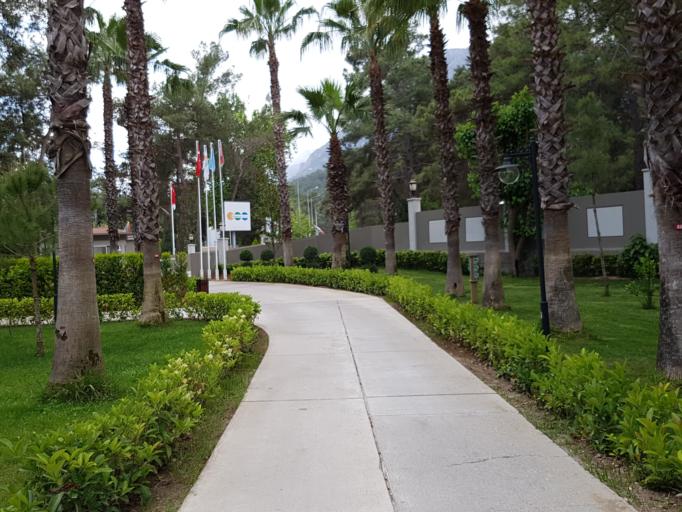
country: TR
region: Antalya
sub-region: Kemer
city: Goeynuek
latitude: 36.6480
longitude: 30.5515
